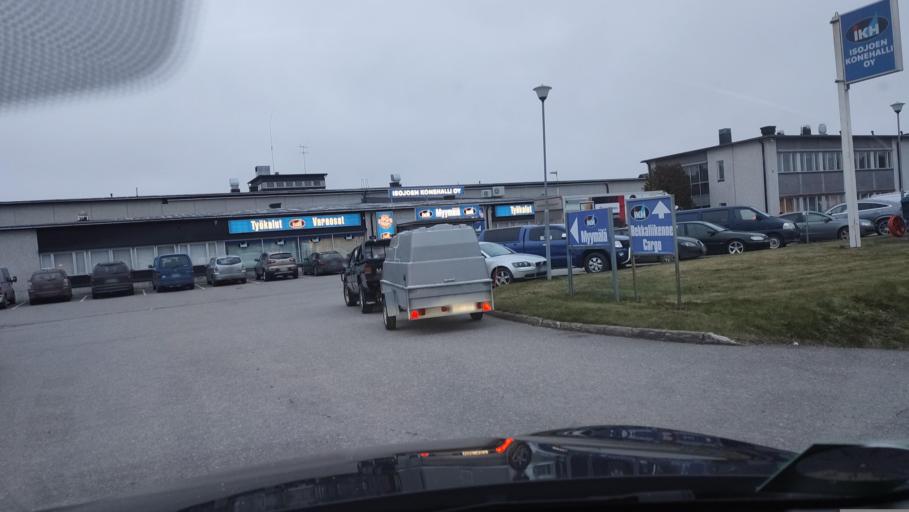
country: FI
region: Southern Ostrobothnia
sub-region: Suupohja
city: Kauhajoki
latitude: 62.4588
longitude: 22.2026
